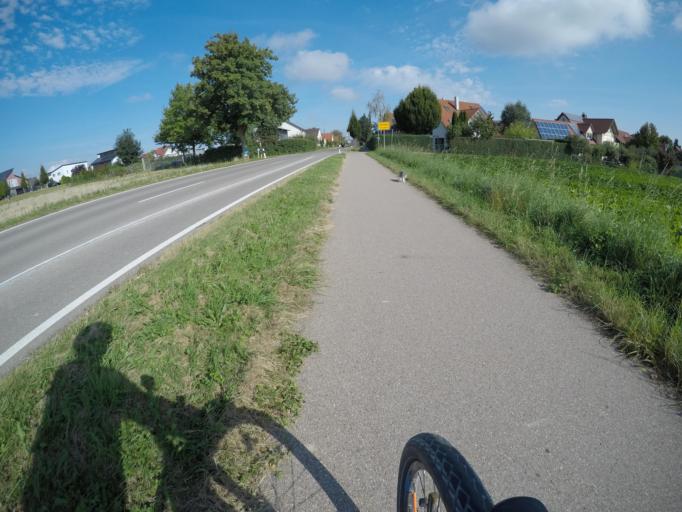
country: DE
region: Bavaria
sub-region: Swabia
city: Allmannshofen
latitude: 48.6094
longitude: 10.8045
